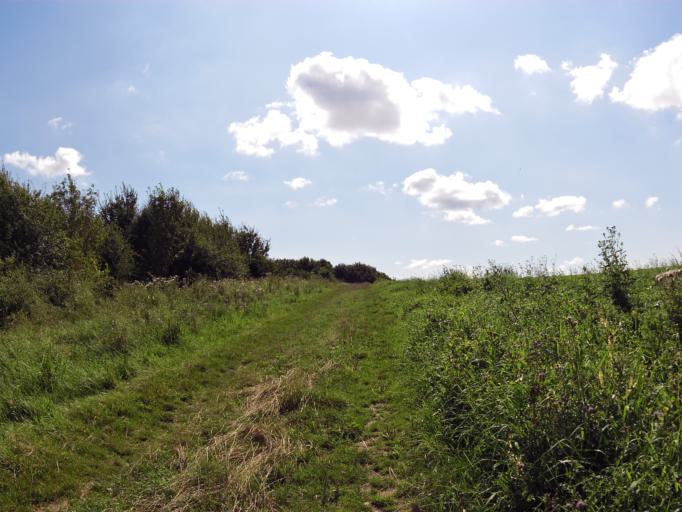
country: NL
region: Limburg
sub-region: Gemeente Kerkrade
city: Kerkrade
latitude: 50.9032
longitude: 6.0684
